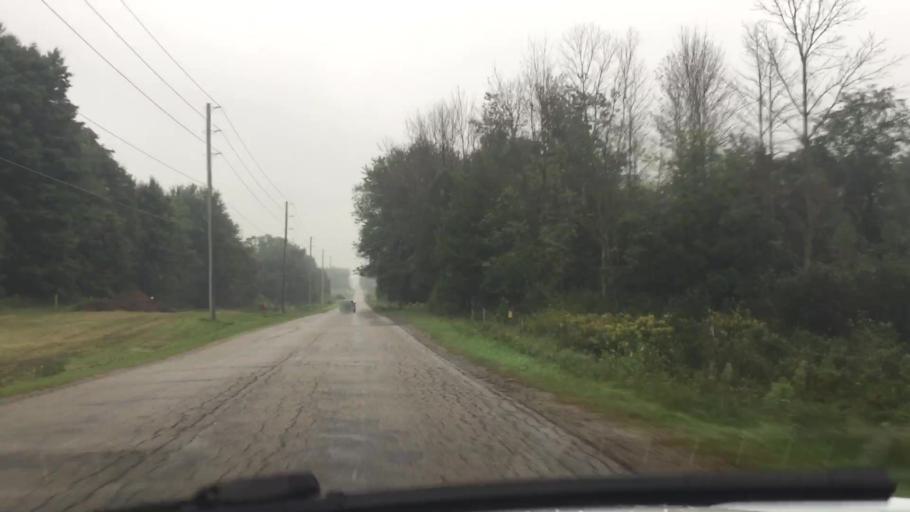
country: CA
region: Ontario
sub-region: Oxford County
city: Woodstock
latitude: 43.1121
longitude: -80.7078
